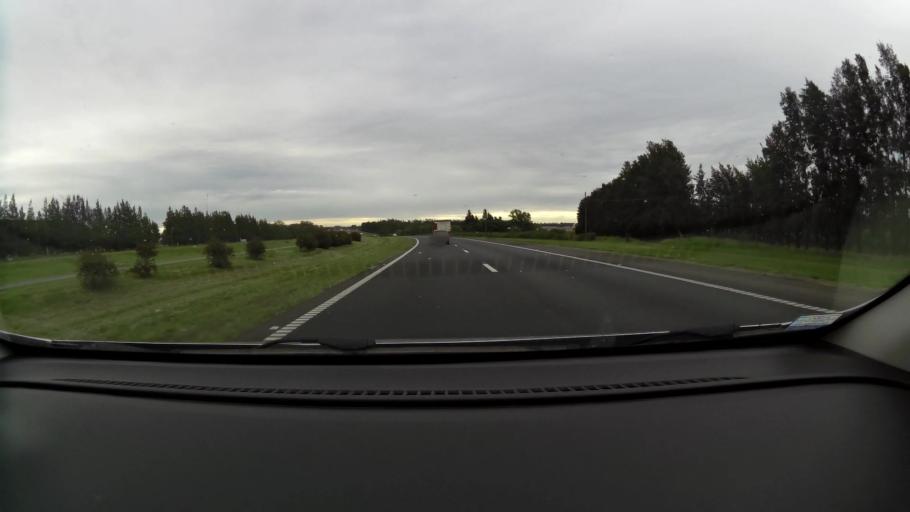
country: AR
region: Buenos Aires
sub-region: Partido de San Pedro
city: San Pedro
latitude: -33.7083
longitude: -59.8340
